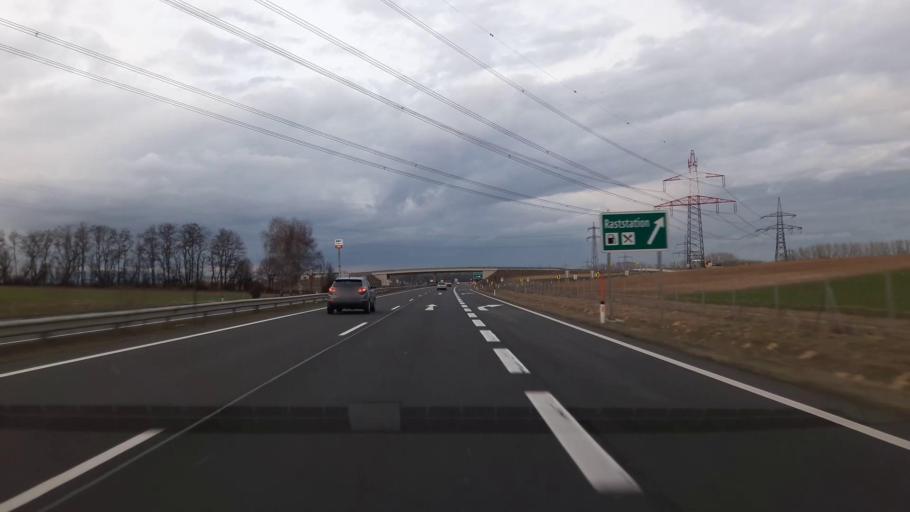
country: AT
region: Burgenland
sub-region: Eisenstadt-Umgebung
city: Hornstein
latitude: 47.8746
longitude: 16.4167
